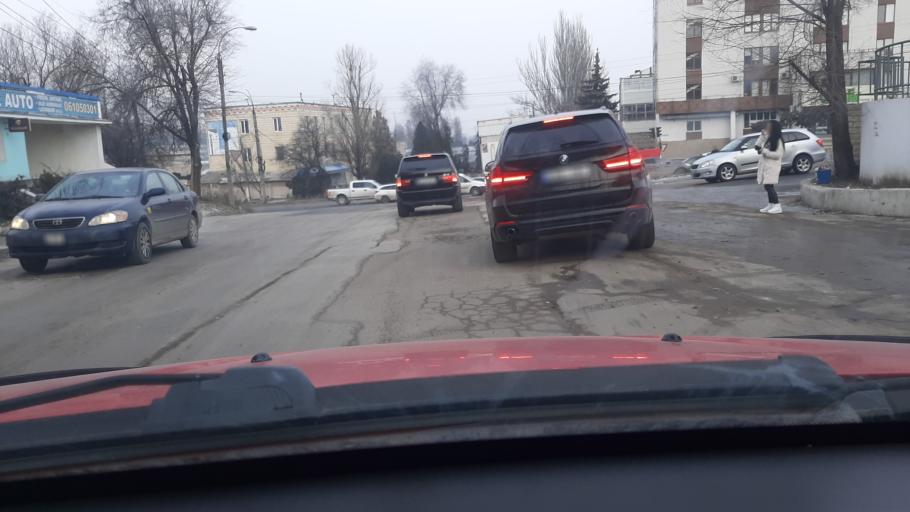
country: MD
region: Chisinau
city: Chisinau
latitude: 46.9789
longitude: 28.8906
